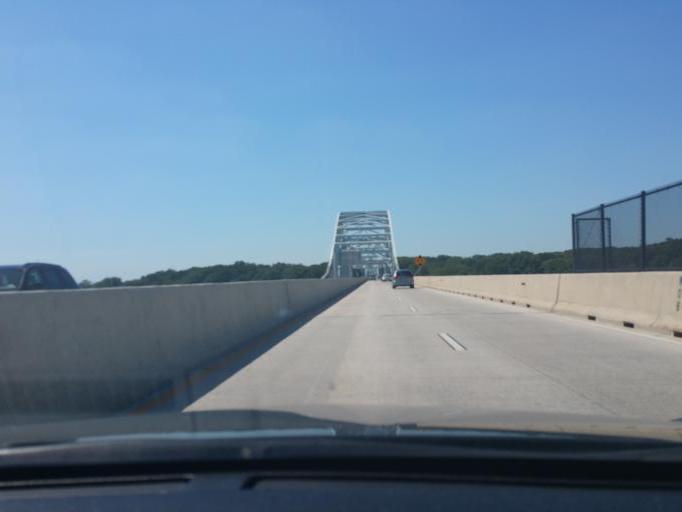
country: US
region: Maryland
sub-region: Cecil County
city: Perryville
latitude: 39.5655
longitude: -76.0796
